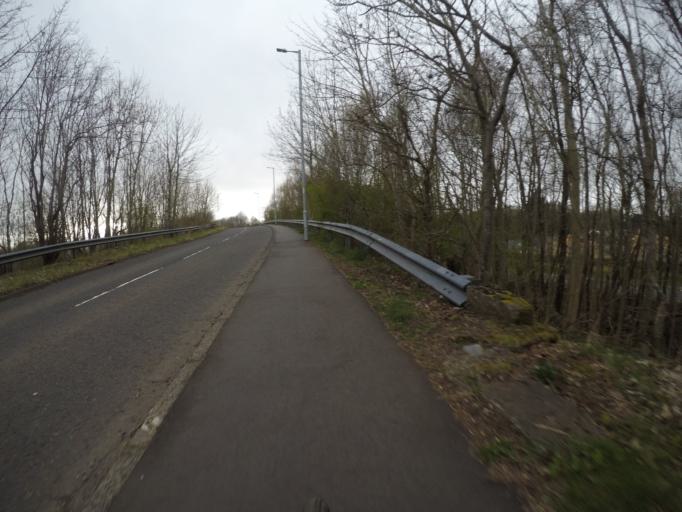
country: GB
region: Scotland
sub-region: North Ayrshire
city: Irvine
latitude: 55.6150
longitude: -4.6438
